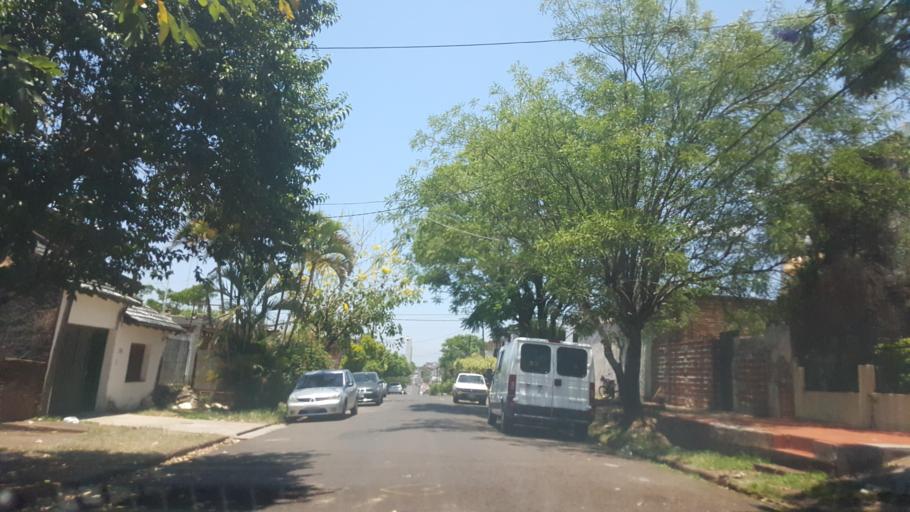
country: AR
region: Misiones
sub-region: Departamento de Capital
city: Posadas
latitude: -27.3729
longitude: -55.8870
